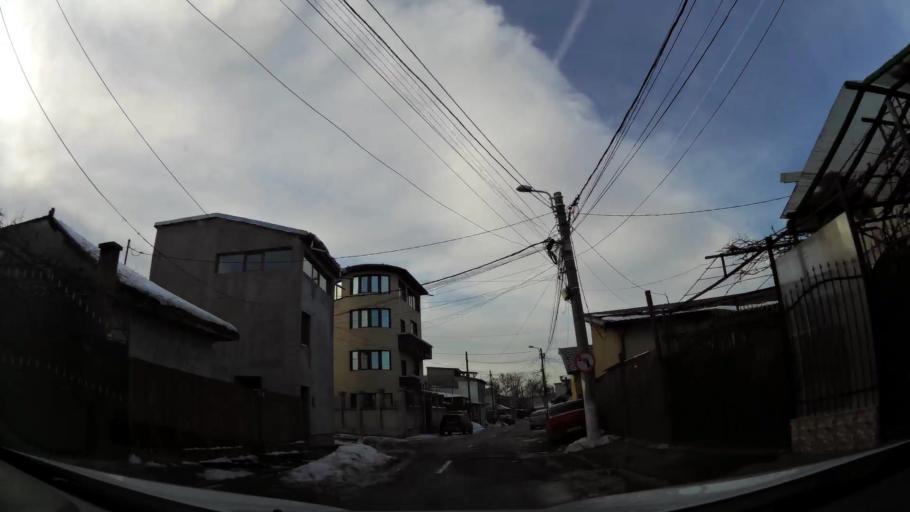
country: RO
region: Bucuresti
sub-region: Municipiul Bucuresti
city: Bucuresti
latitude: 44.3944
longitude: 26.0725
